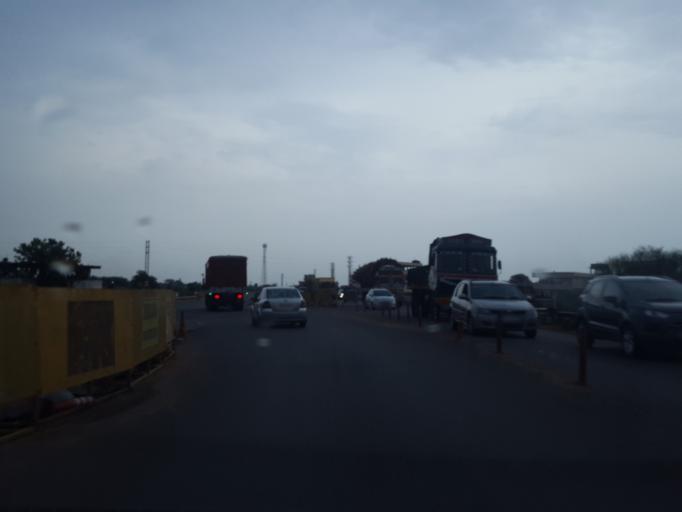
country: IN
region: Telangana
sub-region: Mahbubnagar
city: Farrukhnagar
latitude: 17.1492
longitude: 78.2904
